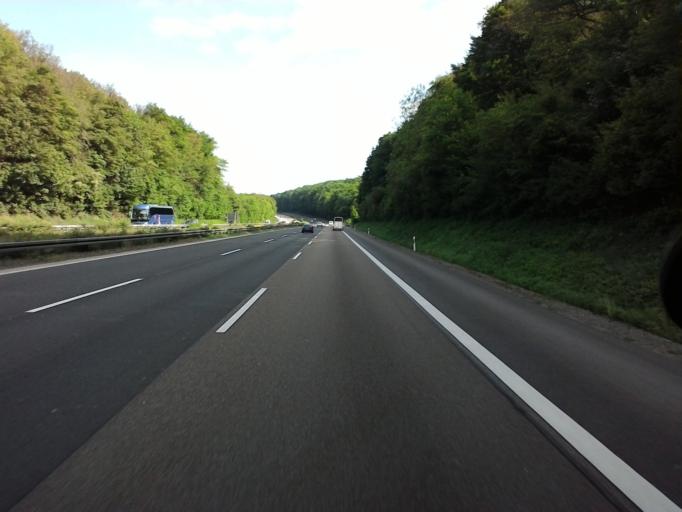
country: DE
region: Hesse
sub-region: Regierungsbezirk Darmstadt
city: Niedernhausen
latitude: 50.1205
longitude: 8.3415
